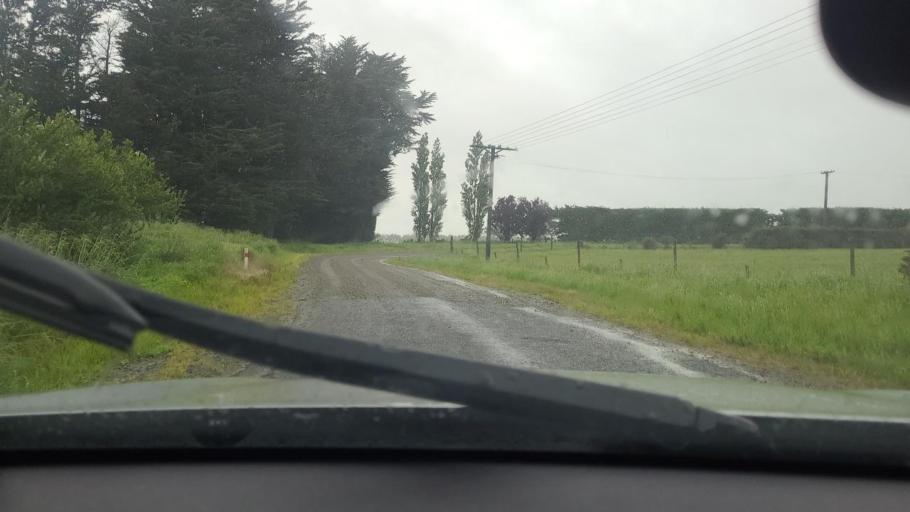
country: NZ
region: Southland
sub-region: Southland District
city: Winton
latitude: -46.1616
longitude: 168.3523
